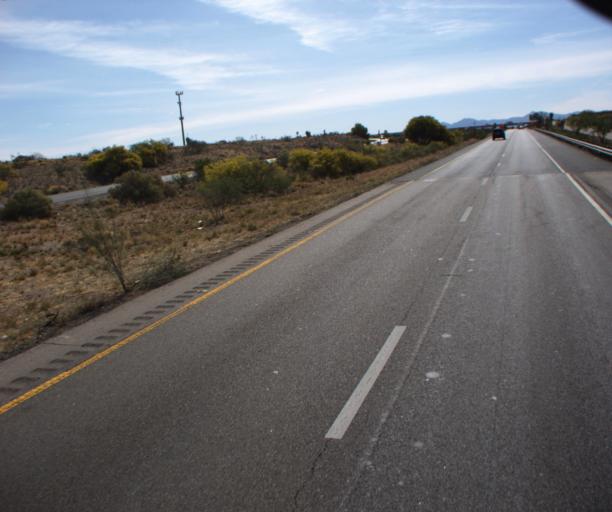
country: US
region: Arizona
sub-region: Pima County
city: Vail
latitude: 32.0113
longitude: -110.6970
